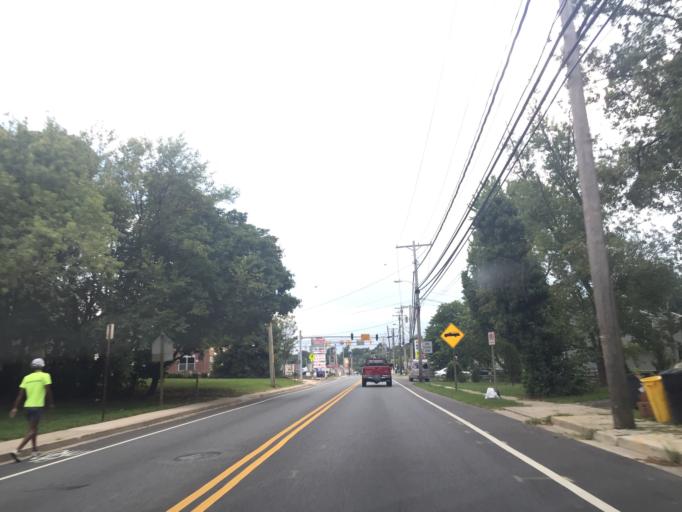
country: US
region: Maryland
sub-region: Anne Arundel County
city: Linthicum
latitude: 39.2029
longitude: -76.6539
